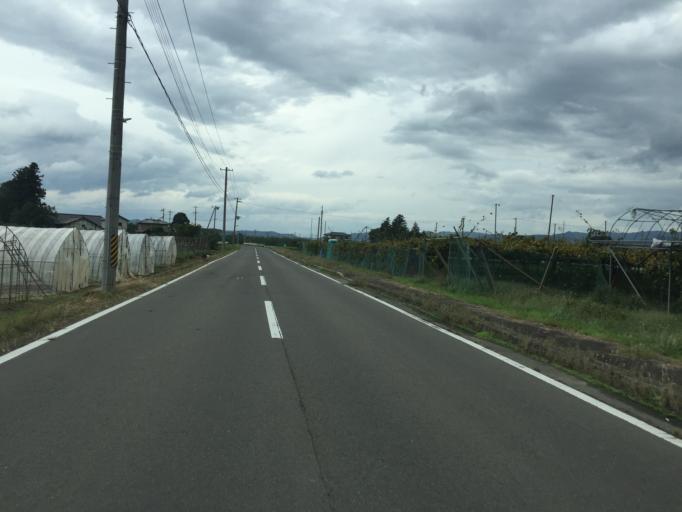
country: JP
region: Fukushima
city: Hobaramachi
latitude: 37.8366
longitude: 140.5647
